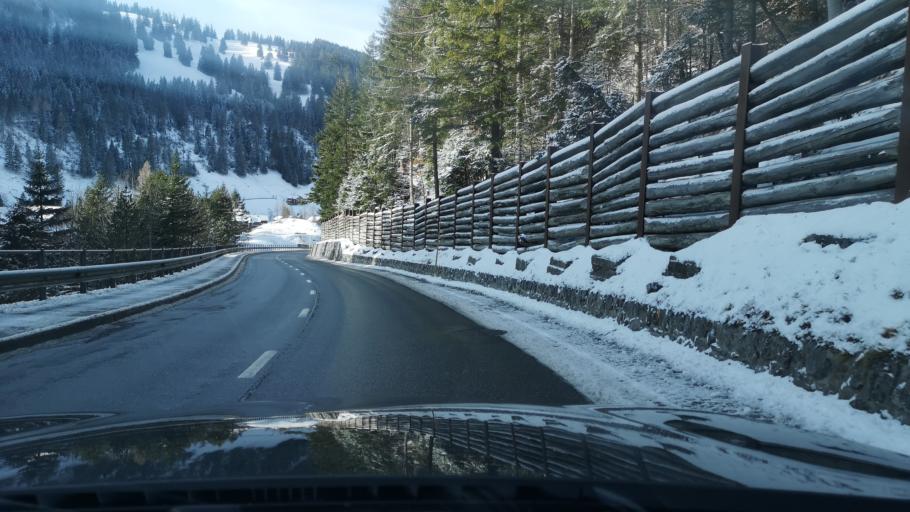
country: LI
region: Triesenberg
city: Triesenberg
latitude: 47.1118
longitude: 9.5804
